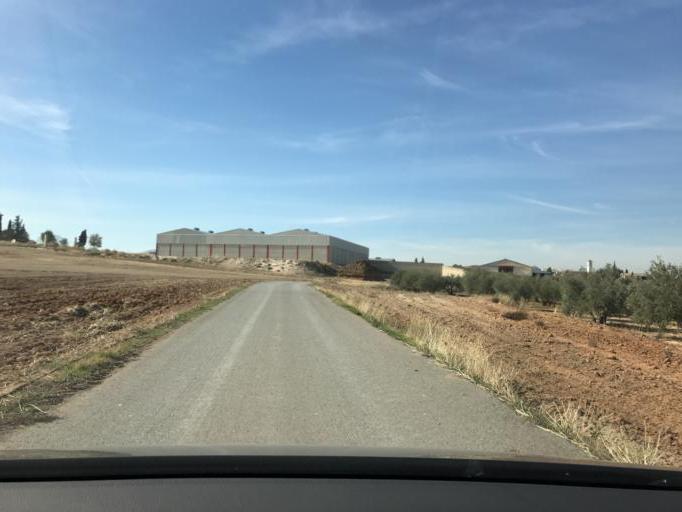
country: ES
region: Andalusia
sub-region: Provincia de Granada
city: Ventas de Huelma
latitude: 37.0835
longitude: -3.8016
